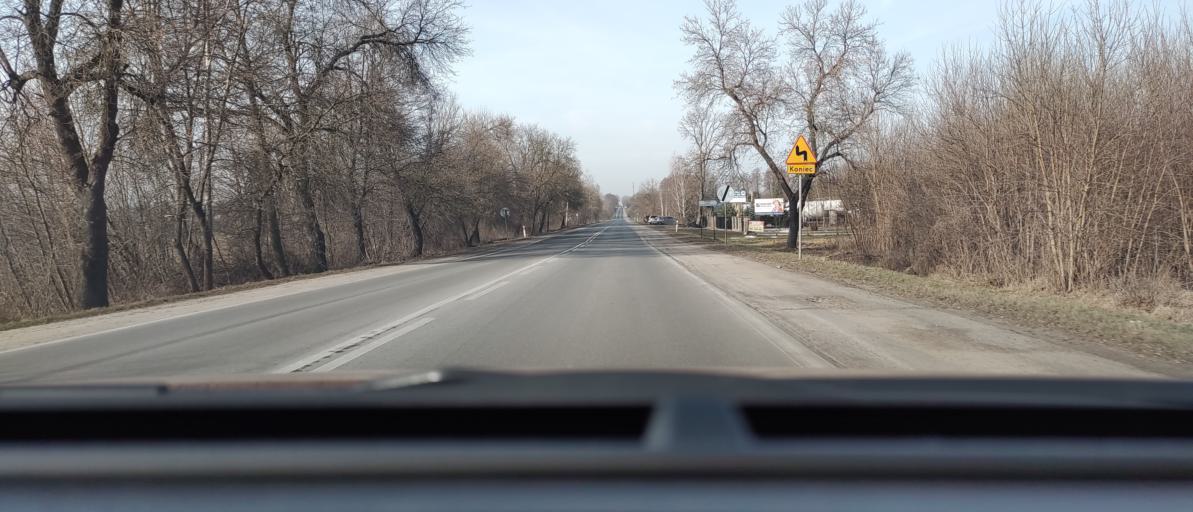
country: PL
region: Masovian Voivodeship
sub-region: Powiat bialobrzeski
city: Bialobrzegi
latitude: 51.6621
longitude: 20.9505
